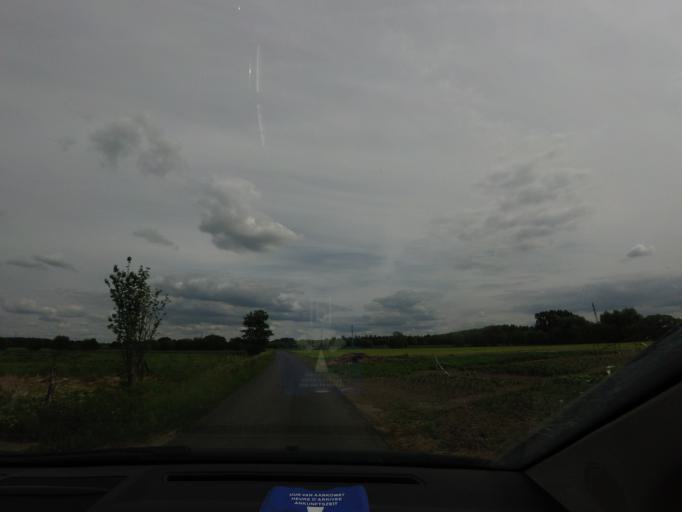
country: BE
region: Flanders
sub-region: Provincie Antwerpen
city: Puurs
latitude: 51.0970
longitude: 4.2748
